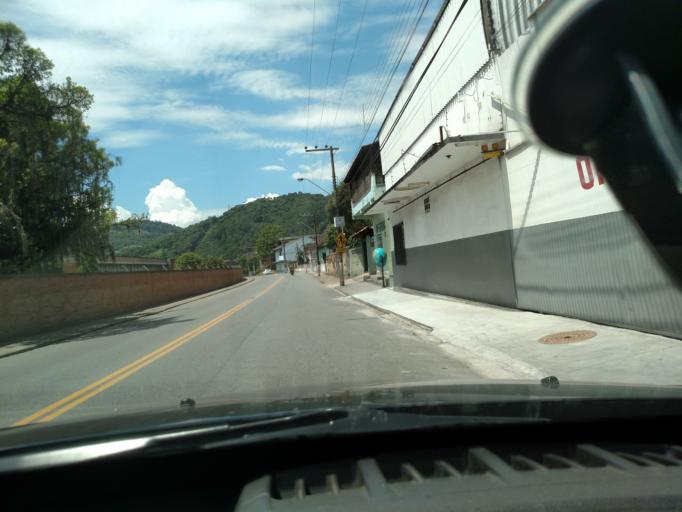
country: BR
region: Santa Catarina
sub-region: Blumenau
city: Blumenau
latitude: -26.9628
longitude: -49.0713
